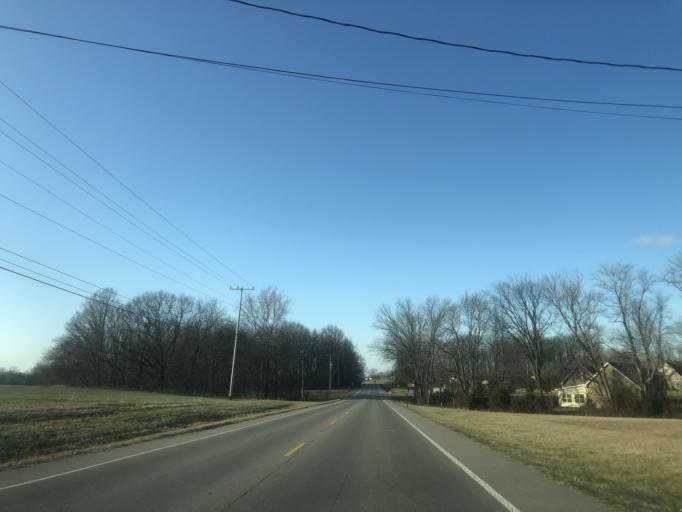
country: US
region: Tennessee
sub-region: Sumner County
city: Portland
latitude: 36.6247
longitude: -86.5565
